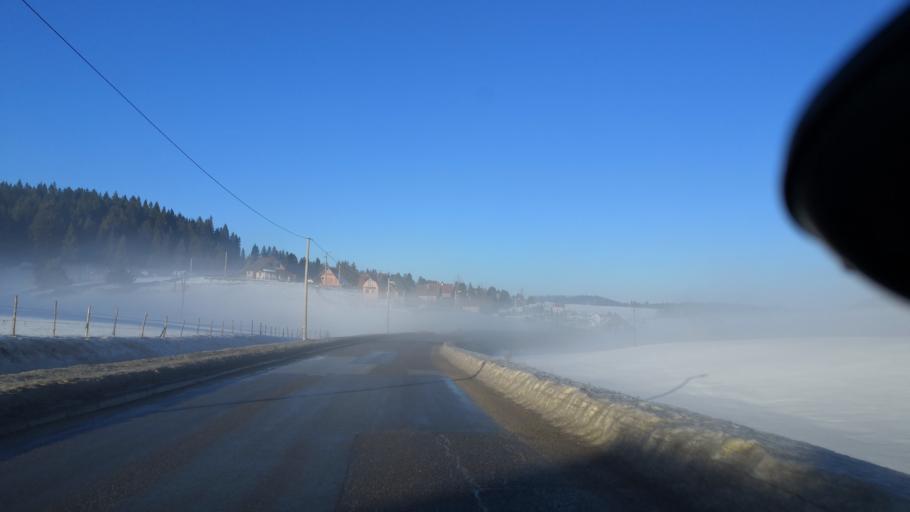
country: BA
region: Republika Srpska
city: Han Pijesak
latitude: 44.0918
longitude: 18.9550
